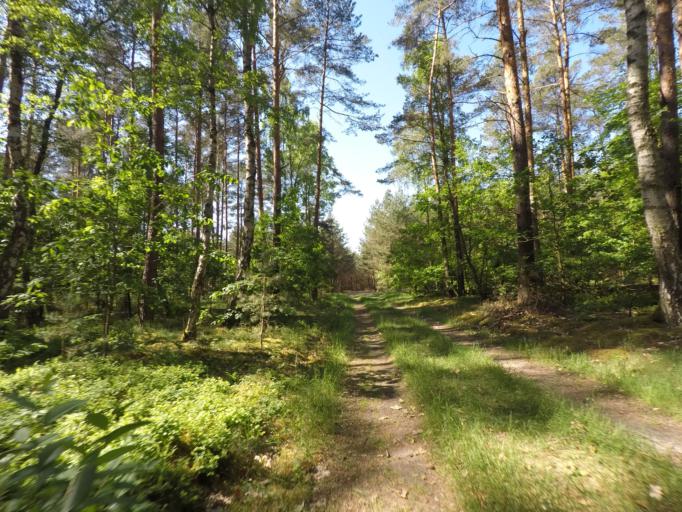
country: DE
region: Brandenburg
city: Melchow
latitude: 52.8271
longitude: 13.7445
